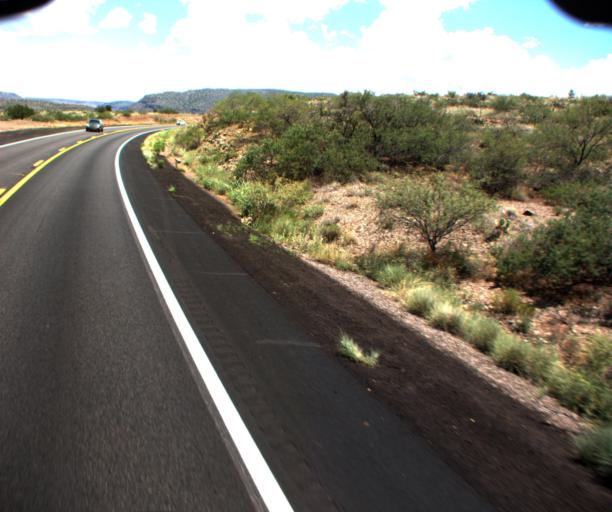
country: US
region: Arizona
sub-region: Yavapai County
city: Camp Verde
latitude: 34.5118
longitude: -111.7496
